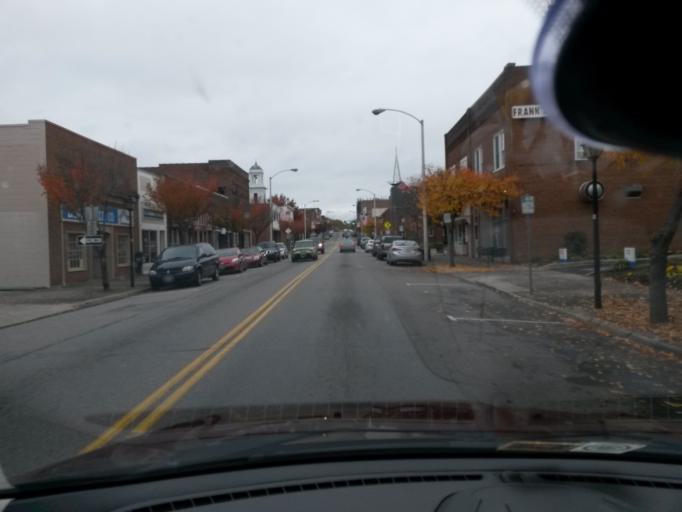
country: US
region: Virginia
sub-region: City of Salem
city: Salem
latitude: 37.2927
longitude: -80.0585
